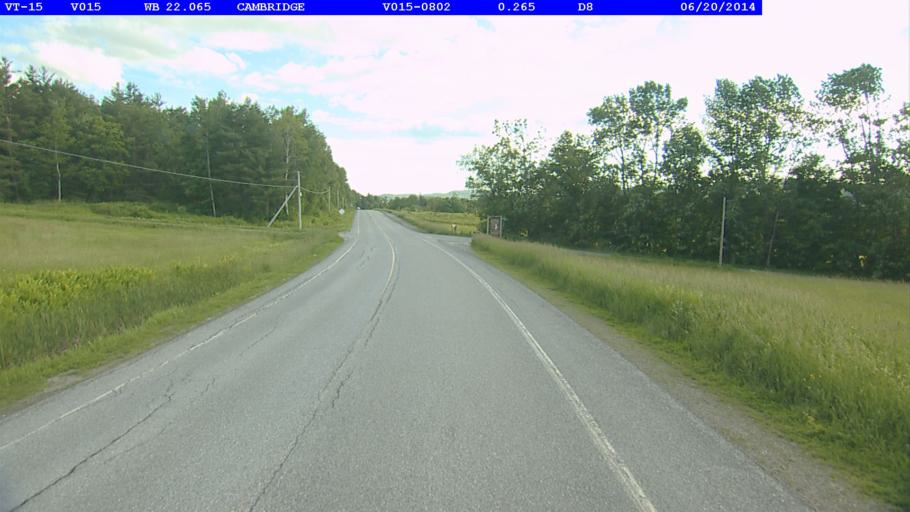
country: US
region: Vermont
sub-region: Chittenden County
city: Jericho
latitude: 44.6351
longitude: -72.9137
